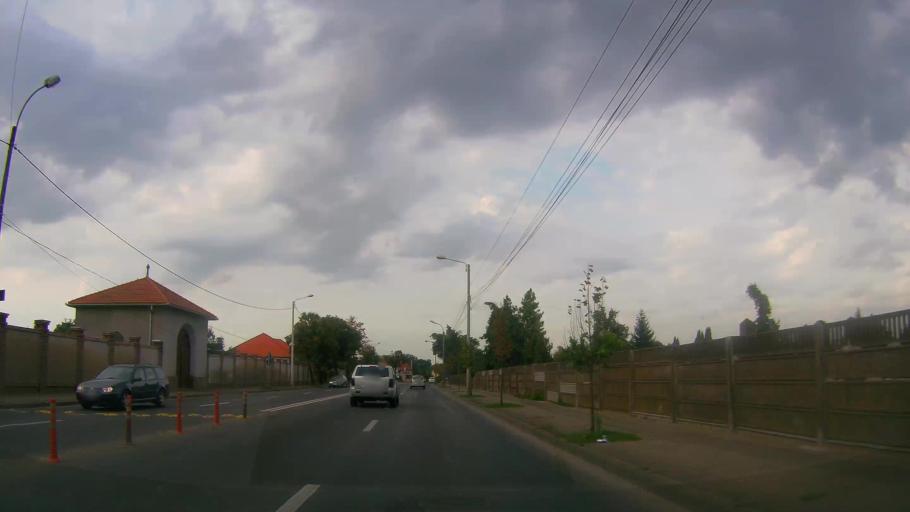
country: RO
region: Satu Mare
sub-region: Municipiul Satu Mare
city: Satu Mare
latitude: 47.7911
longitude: 22.8915
